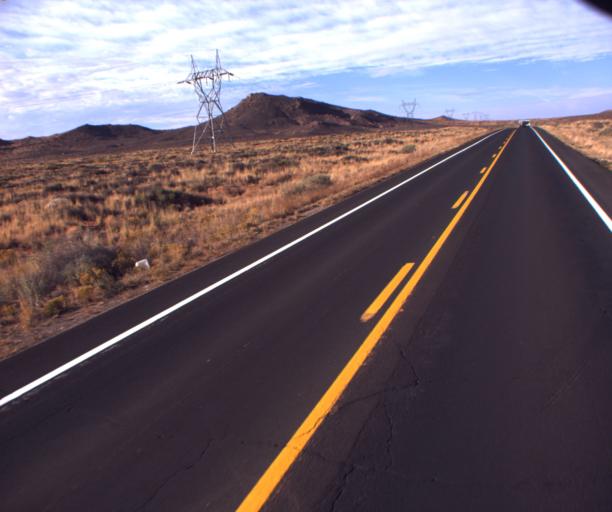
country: US
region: Arizona
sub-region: Apache County
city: Lukachukai
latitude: 36.9622
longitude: -109.4853
